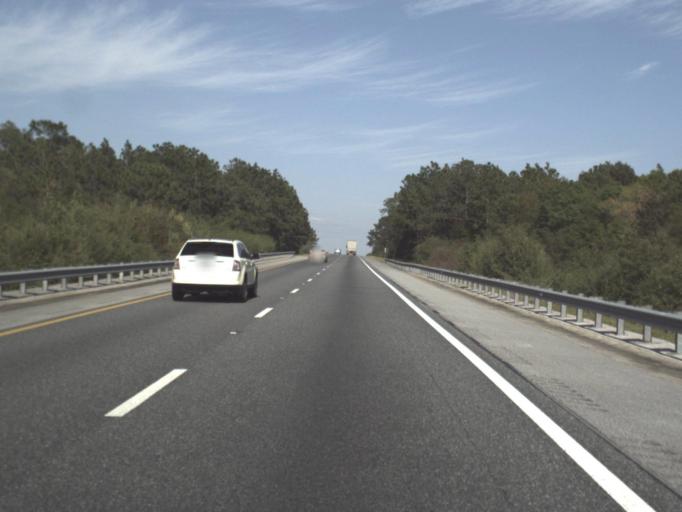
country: US
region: Florida
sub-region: Okaloosa County
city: Crestview
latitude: 30.7138
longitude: -86.6210
